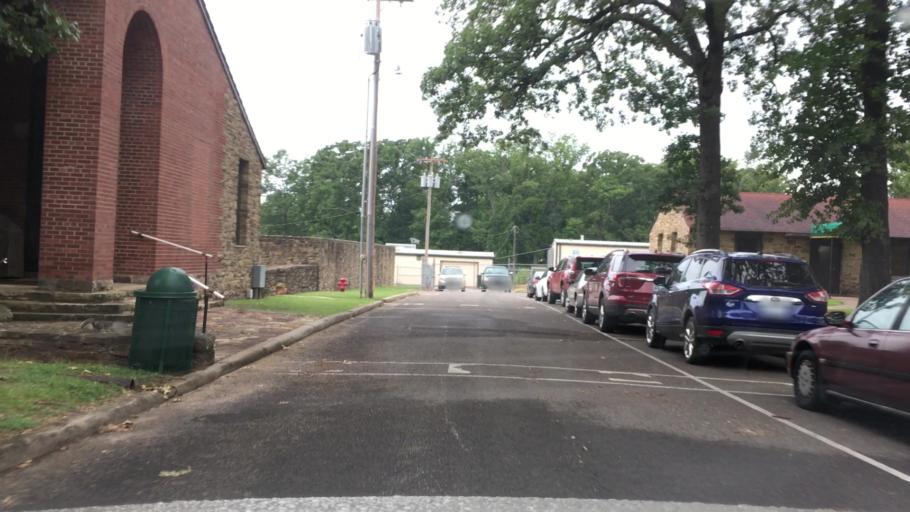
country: US
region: Oklahoma
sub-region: Cherokee County
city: Tahlequah
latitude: 35.9255
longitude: -94.9672
